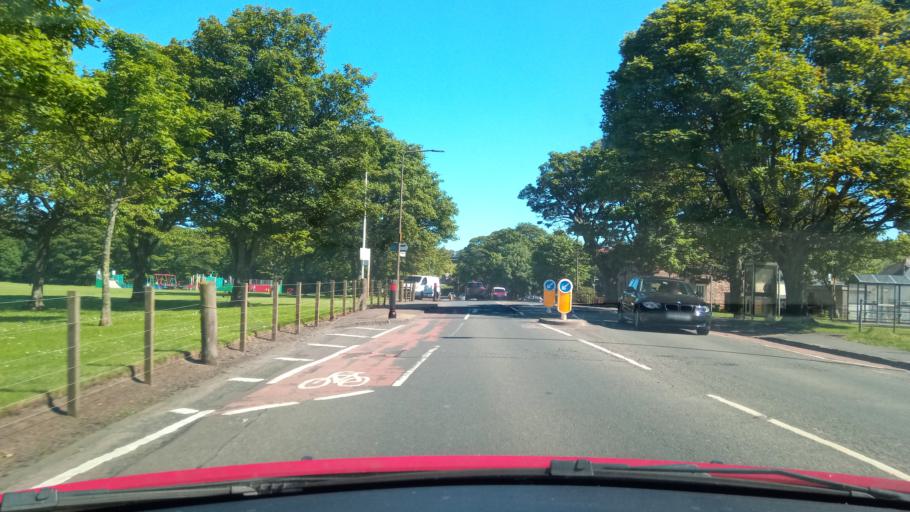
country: GB
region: Scotland
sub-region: East Lothian
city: North Berwick
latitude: 56.0539
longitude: -2.7077
